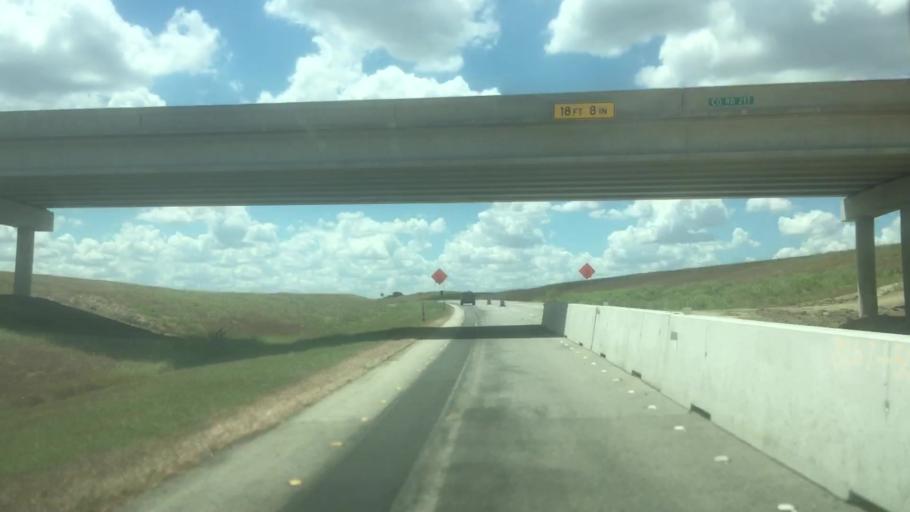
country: US
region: Texas
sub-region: Caldwell County
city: Lockhart
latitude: 29.8528
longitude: -97.7206
